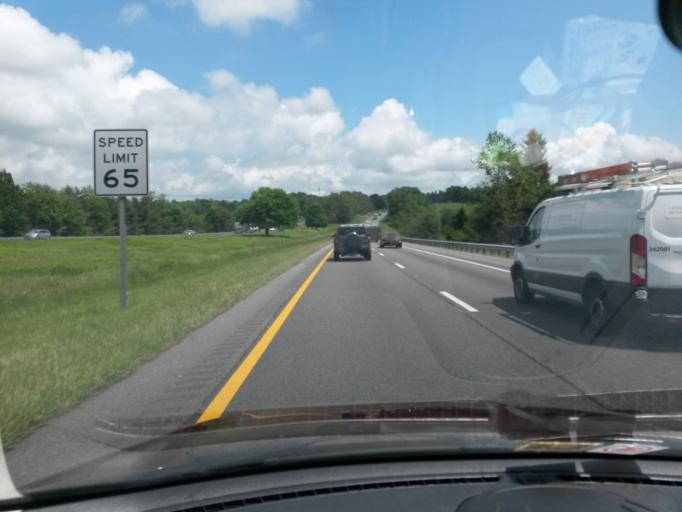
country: US
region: Virginia
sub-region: Carroll County
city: Woodlawn
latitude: 36.7767
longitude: -80.8194
